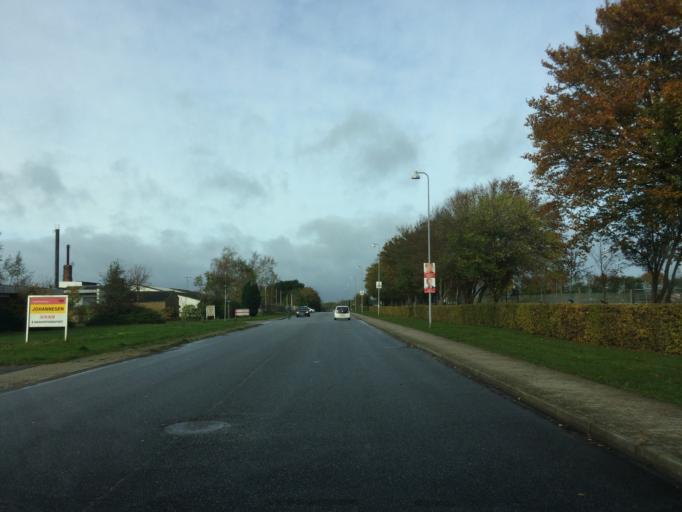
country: DK
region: South Denmark
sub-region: Fredericia Kommune
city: Fredericia
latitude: 55.5774
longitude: 9.7465
